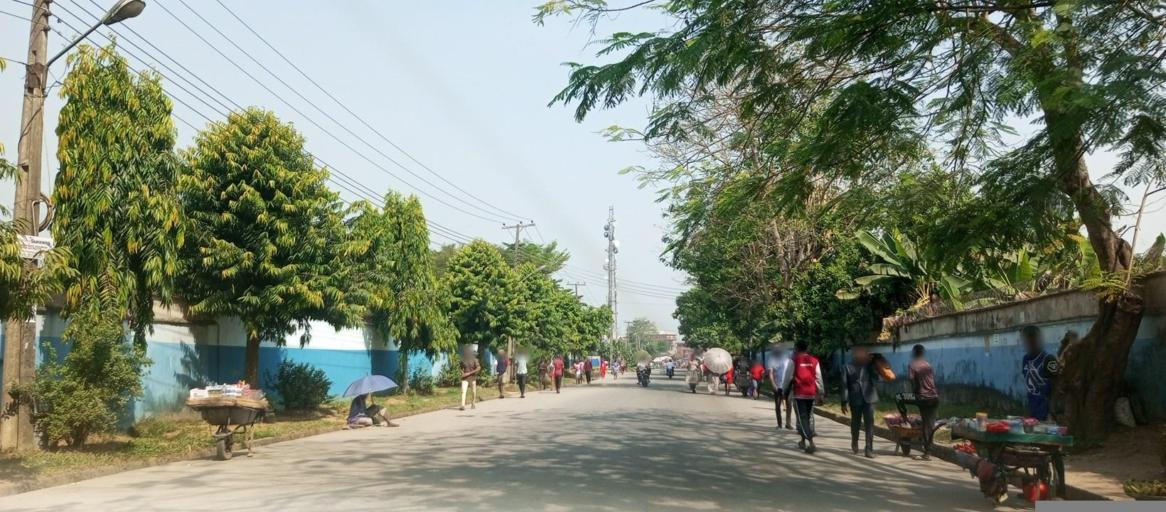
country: NG
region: Rivers
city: Emuoha
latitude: 4.8999
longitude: 6.9066
